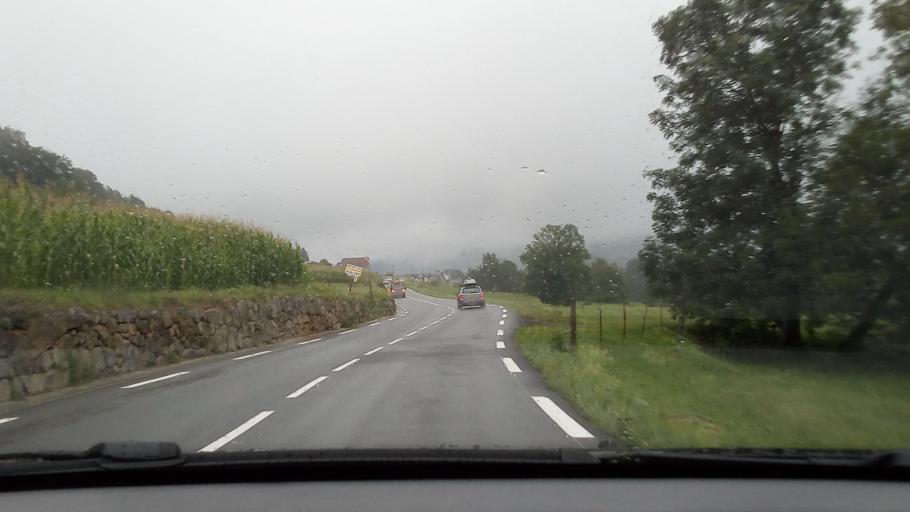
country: FR
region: Midi-Pyrenees
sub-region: Departement des Hautes-Pyrenees
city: Argeles-Gazost
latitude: 42.9865
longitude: -0.1403
